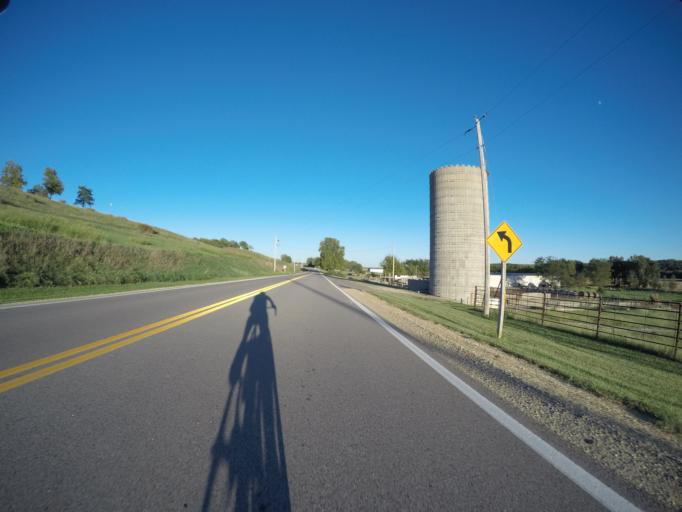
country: US
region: Kansas
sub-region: Riley County
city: Ogden
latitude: 39.2307
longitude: -96.7412
